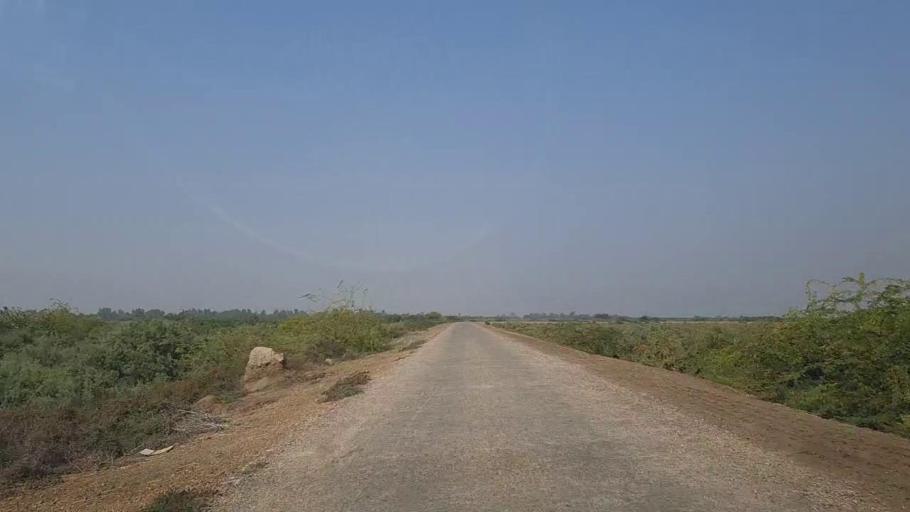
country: PK
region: Sindh
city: Keti Bandar
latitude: 24.2280
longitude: 67.6754
